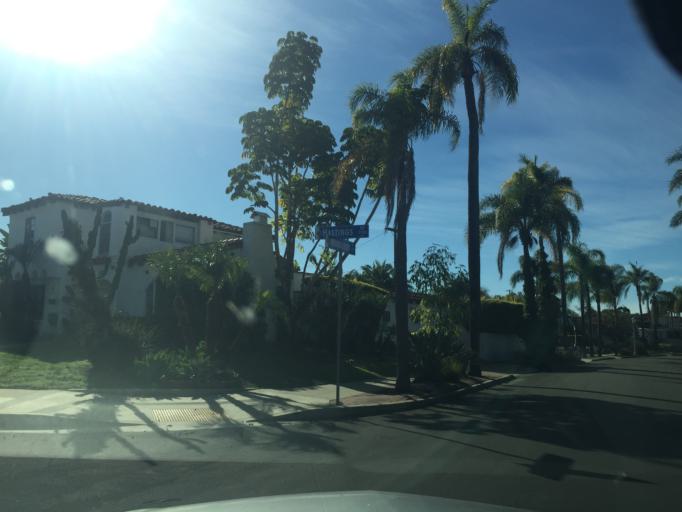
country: US
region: California
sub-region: San Diego County
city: Lemon Grove
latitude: 32.7716
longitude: -117.1033
